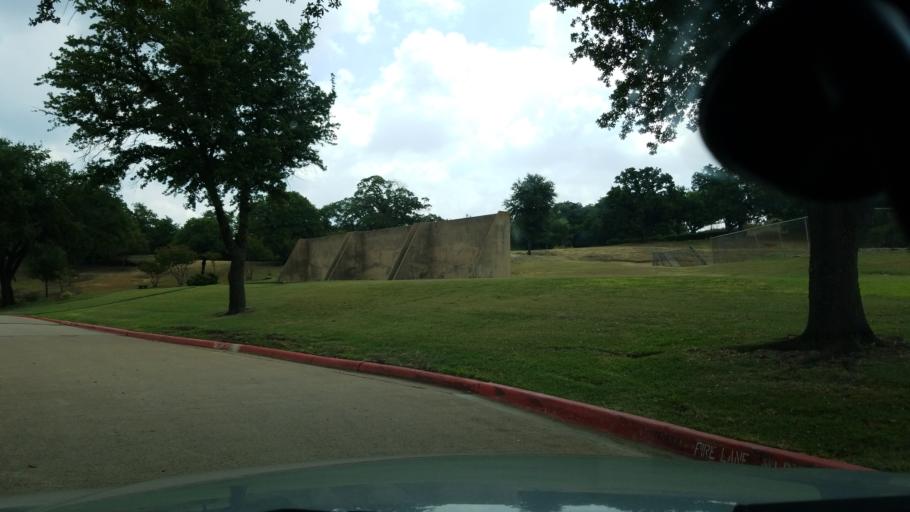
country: US
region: Texas
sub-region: Dallas County
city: Irving
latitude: 32.8489
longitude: -96.9224
